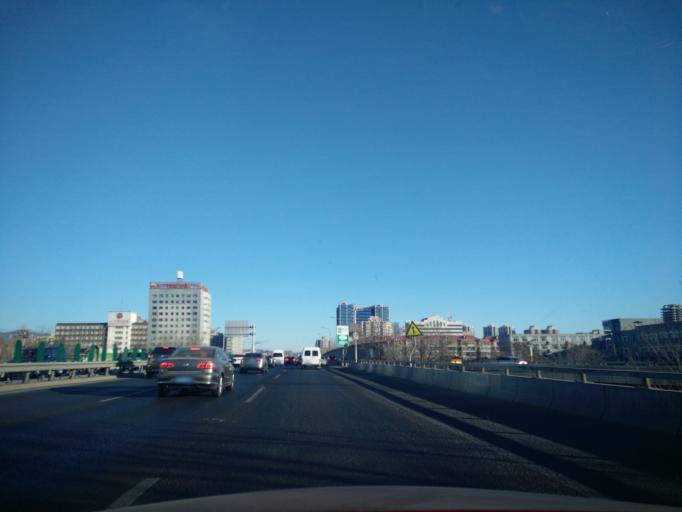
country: CN
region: Beijing
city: Lugu
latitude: 39.8952
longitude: 116.2051
